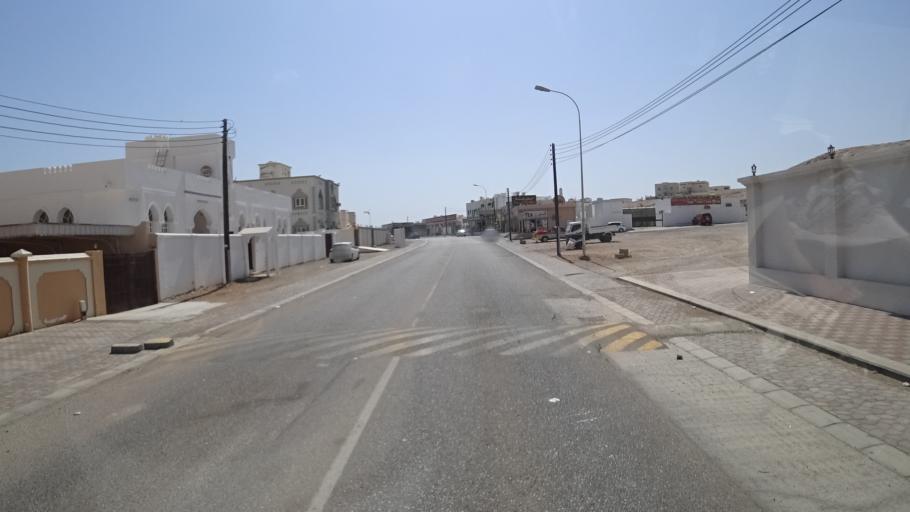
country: OM
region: Ash Sharqiyah
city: Sur
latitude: 22.5667
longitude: 59.5515
